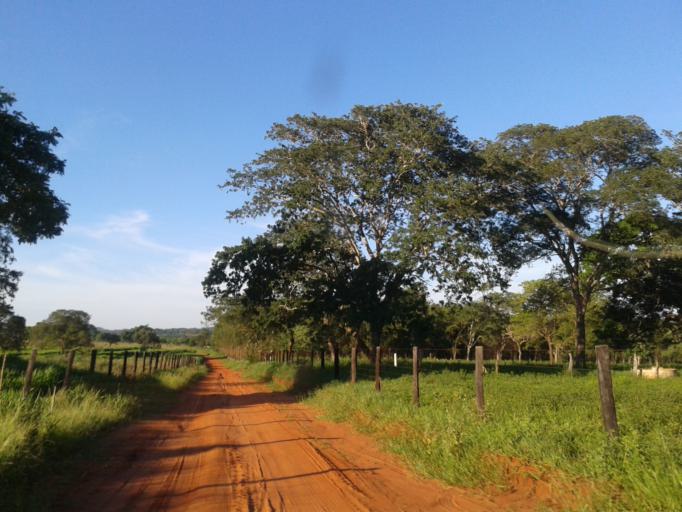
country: BR
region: Minas Gerais
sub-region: Santa Vitoria
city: Santa Vitoria
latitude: -18.9298
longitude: -49.8535
